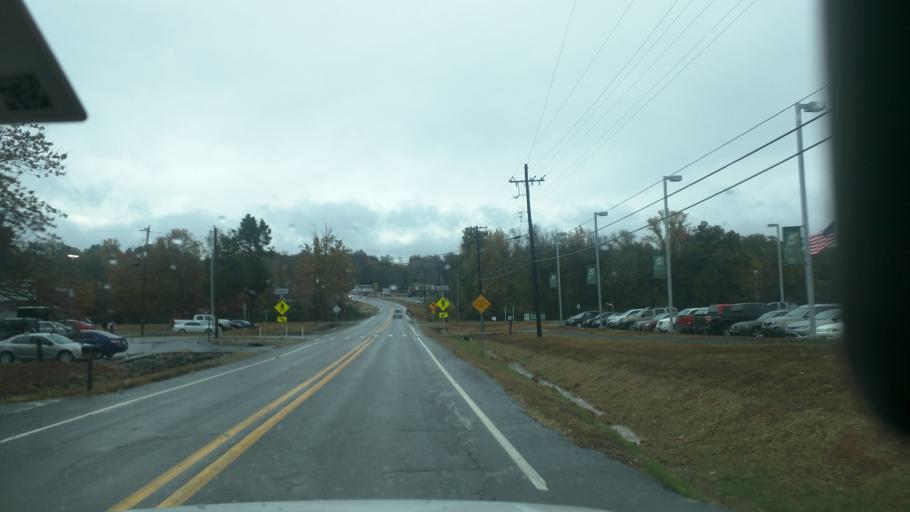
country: US
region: Arkansas
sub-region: Franklin County
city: Ozark
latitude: 35.4970
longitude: -93.8435
